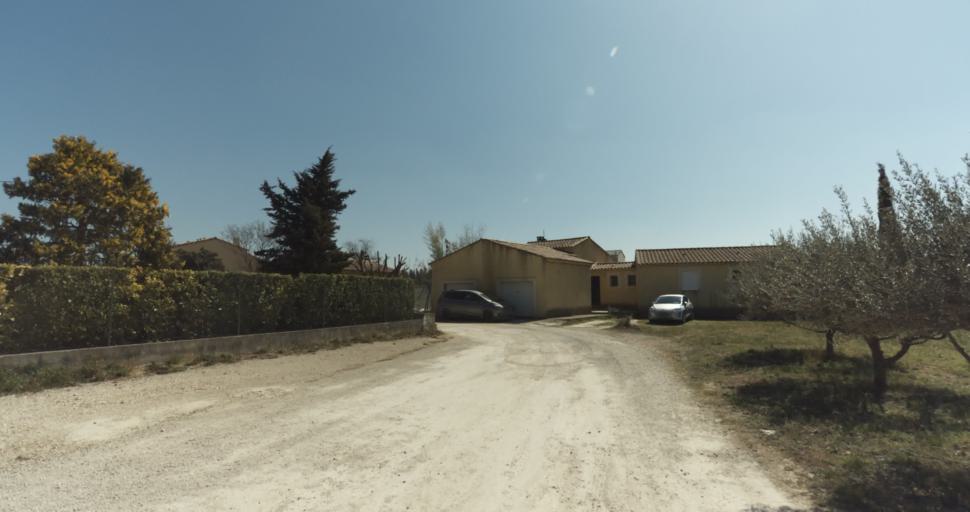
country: FR
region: Provence-Alpes-Cote d'Azur
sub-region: Departement des Bouches-du-Rhone
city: Pelissanne
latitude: 43.6269
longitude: 5.1592
